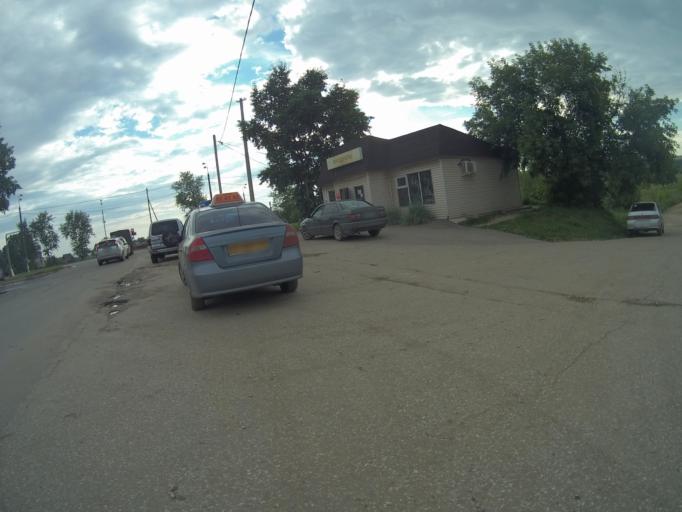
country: RU
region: Vladimir
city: Kommunar
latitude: 56.1109
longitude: 40.4295
